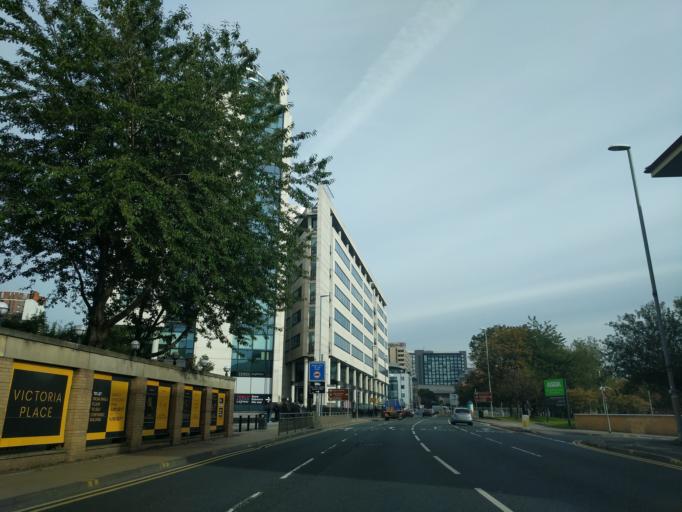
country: GB
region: England
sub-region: City and Borough of Leeds
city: Leeds
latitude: 53.7906
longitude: -1.5474
